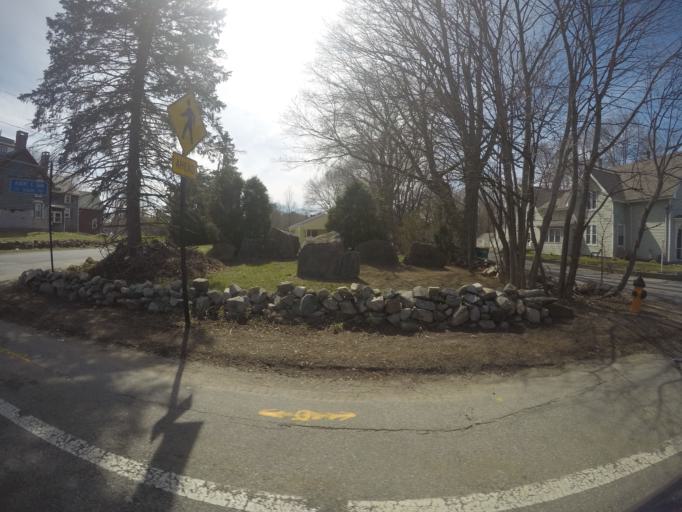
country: US
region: Massachusetts
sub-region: Bristol County
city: Easton
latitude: 42.0527
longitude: -71.0849
